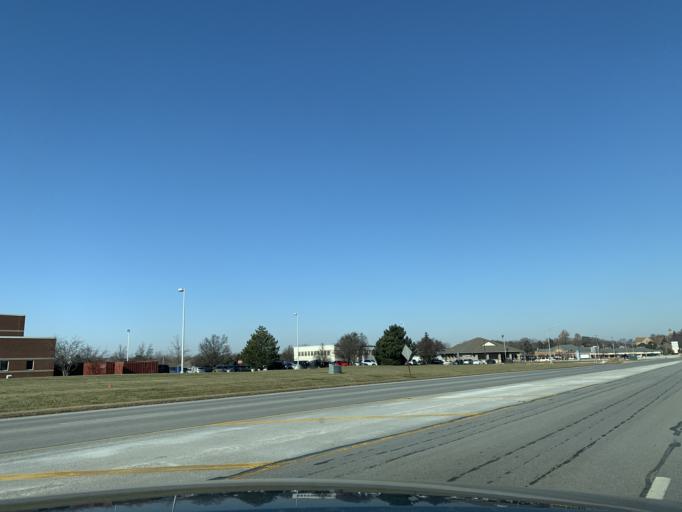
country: US
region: Indiana
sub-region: Lake County
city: Saint John
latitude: 41.4428
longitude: -87.4699
